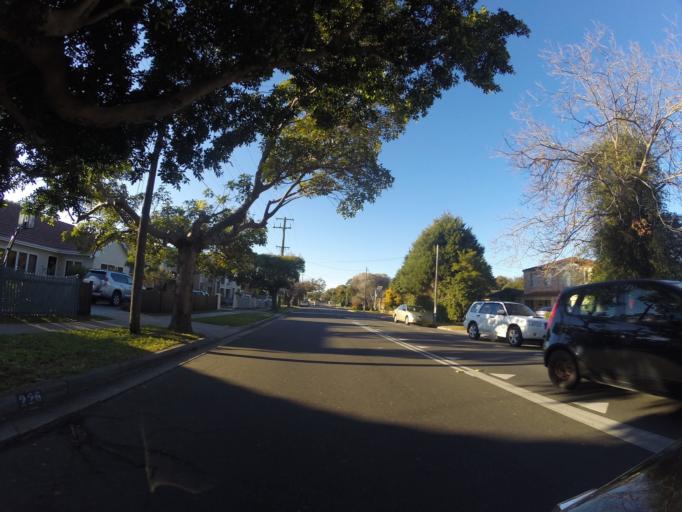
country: AU
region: New South Wales
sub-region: Sutherland Shire
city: Gymea Bay
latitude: -34.0471
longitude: 151.0846
